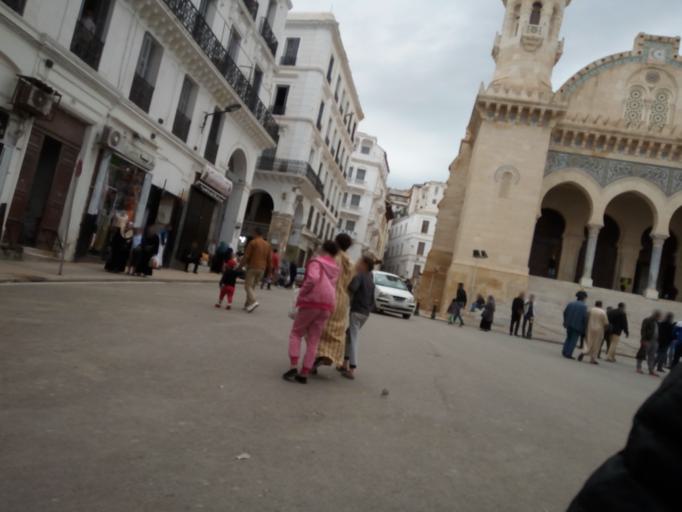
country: DZ
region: Alger
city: Algiers
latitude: 36.7848
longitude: 3.0615
